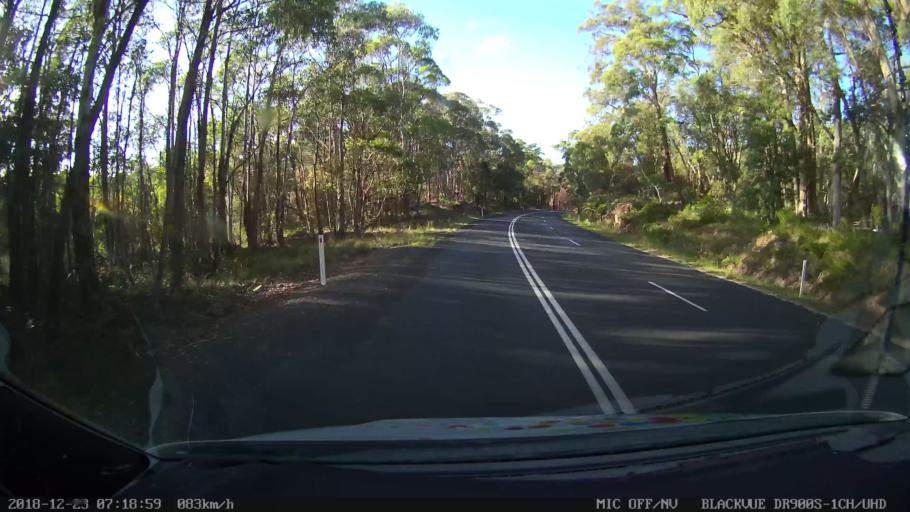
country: AU
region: New South Wales
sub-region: Bellingen
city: Dorrigo
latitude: -30.4814
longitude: 152.2913
